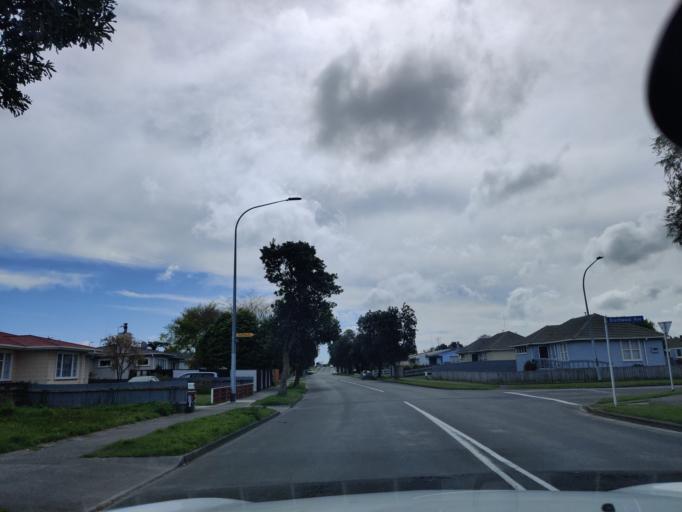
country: NZ
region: Manawatu-Wanganui
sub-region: Palmerston North City
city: Palmerston North
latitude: -40.3588
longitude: 175.5859
